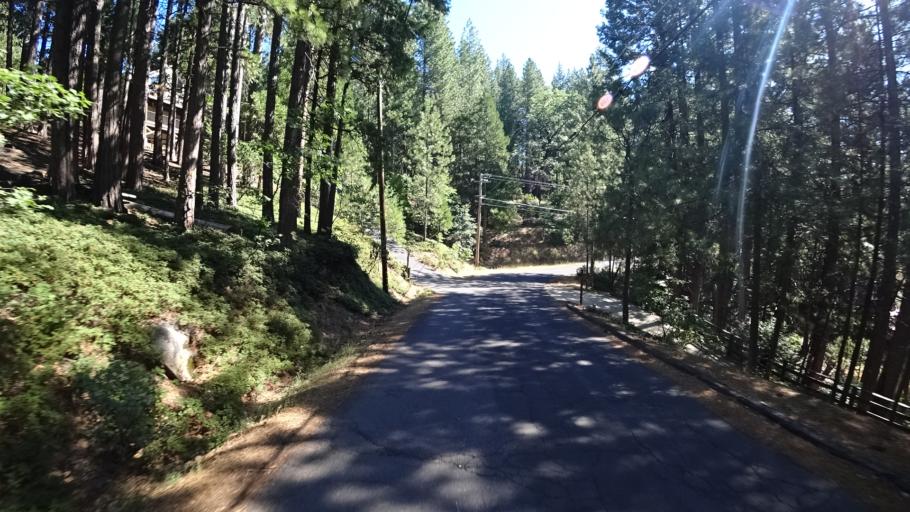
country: US
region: California
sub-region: Calaveras County
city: Arnold
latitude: 38.2439
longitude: -120.3678
